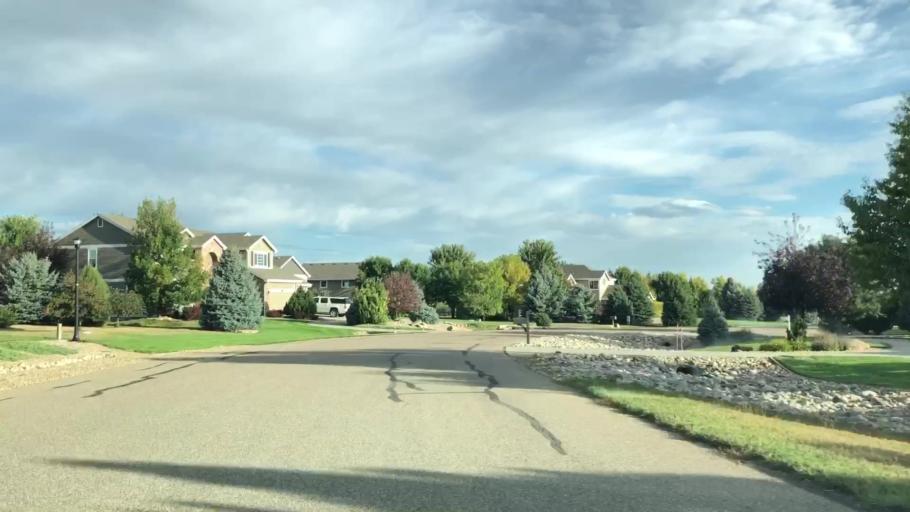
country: US
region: Colorado
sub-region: Weld County
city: Windsor
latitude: 40.4399
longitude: -104.9618
